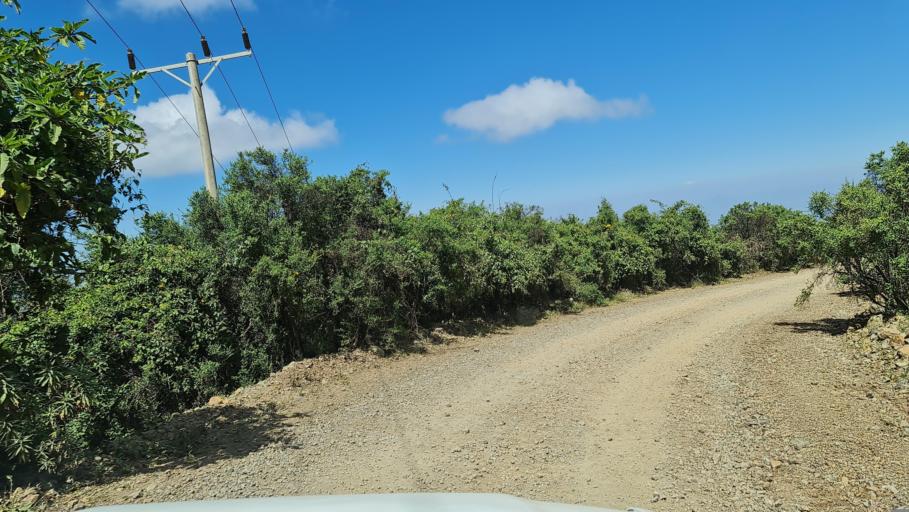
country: ET
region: Amhara
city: Debark'
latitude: 13.2279
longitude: 38.0253
